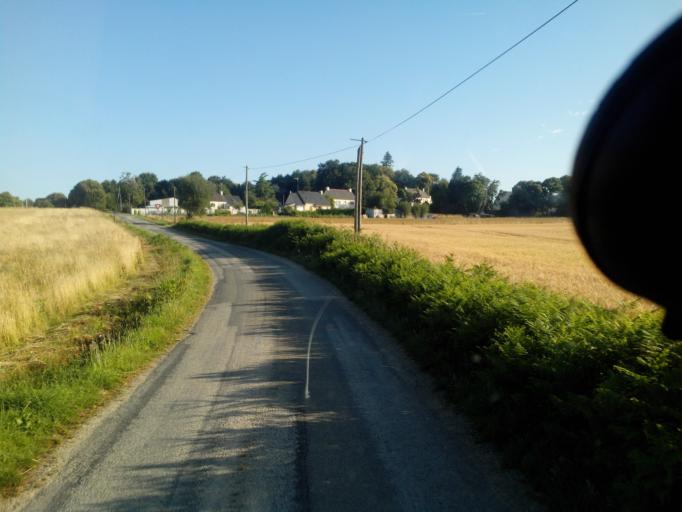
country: FR
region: Brittany
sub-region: Departement du Morbihan
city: Meneac
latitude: 48.1323
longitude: -2.4687
